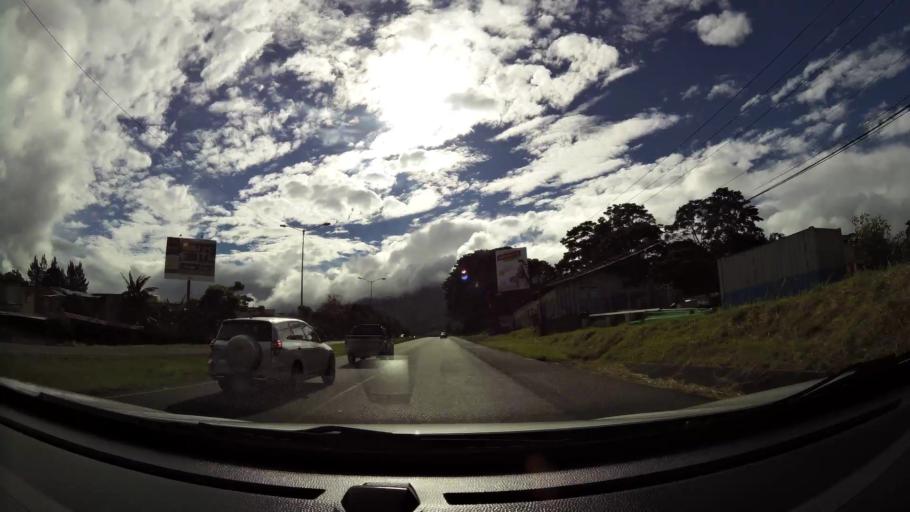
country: CR
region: Cartago
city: San Diego
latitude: 9.9045
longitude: -84.0106
